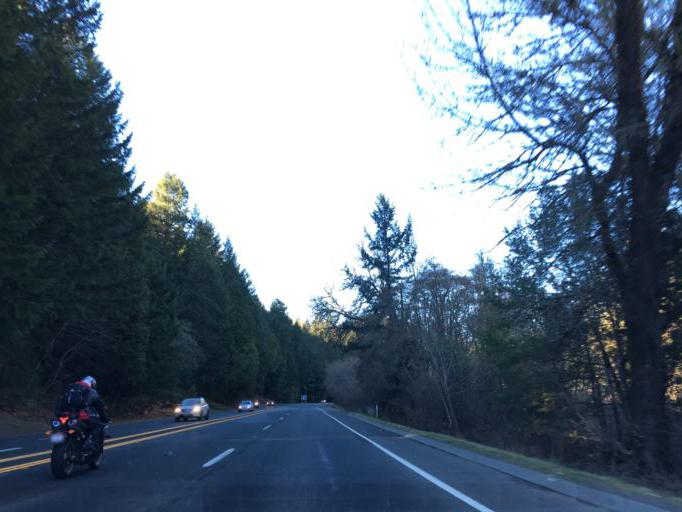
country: US
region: California
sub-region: Mendocino County
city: Laytonville
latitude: 39.5874
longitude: -123.4494
